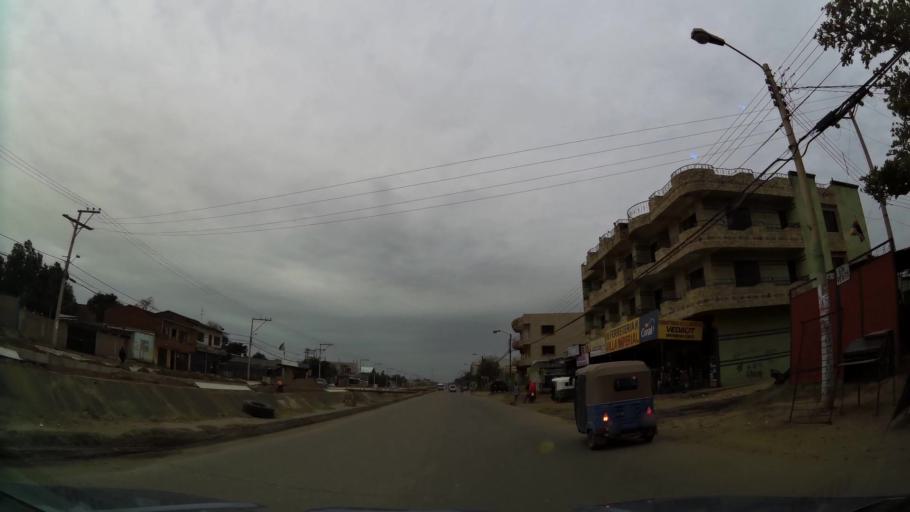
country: BO
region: Santa Cruz
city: Santa Cruz de la Sierra
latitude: -17.8557
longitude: -63.1783
